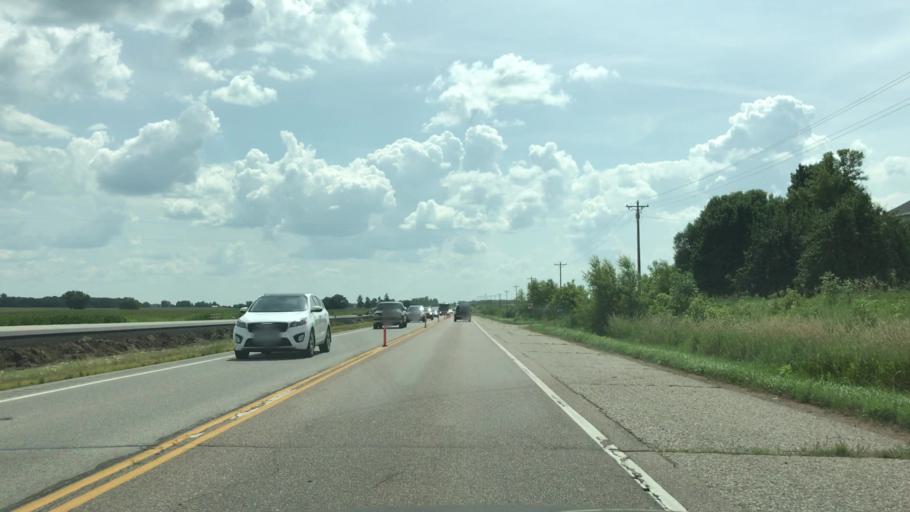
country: US
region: Minnesota
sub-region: Scott County
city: Belle Plaine
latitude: 44.5761
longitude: -93.8396
